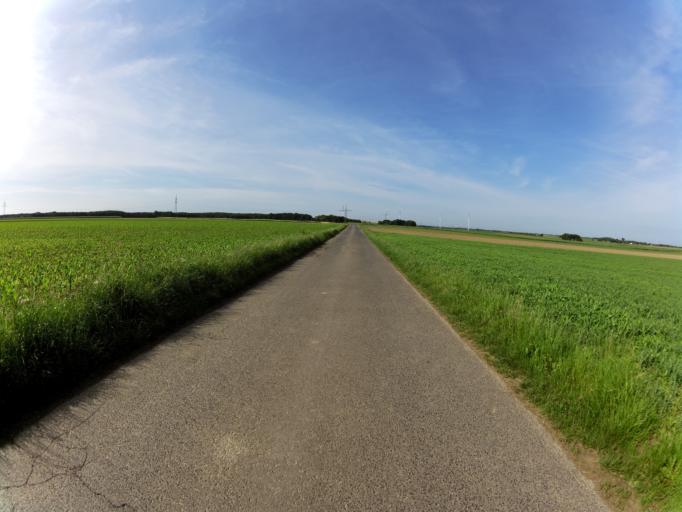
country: DE
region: North Rhine-Westphalia
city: Geilenkirchen
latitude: 51.0049
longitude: 6.0744
